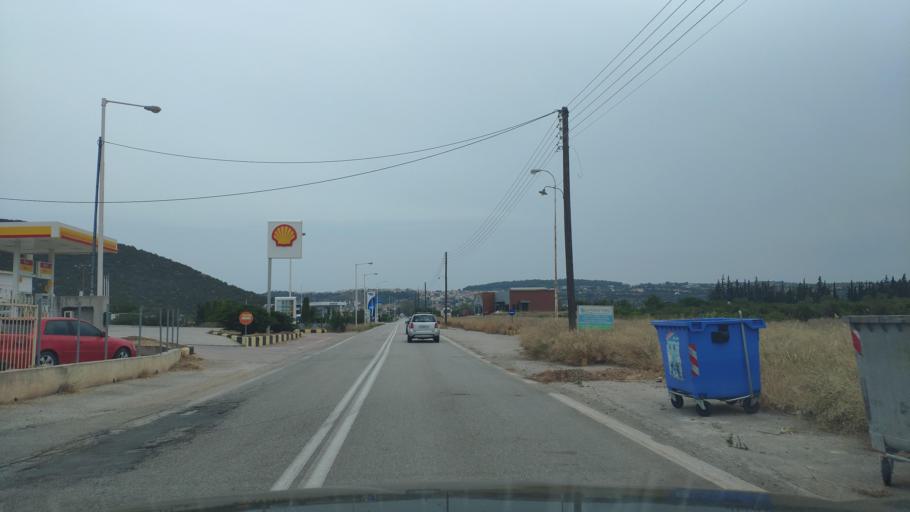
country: GR
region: Peloponnese
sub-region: Nomos Argolidos
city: Kranidi
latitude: 37.4036
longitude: 23.1550
